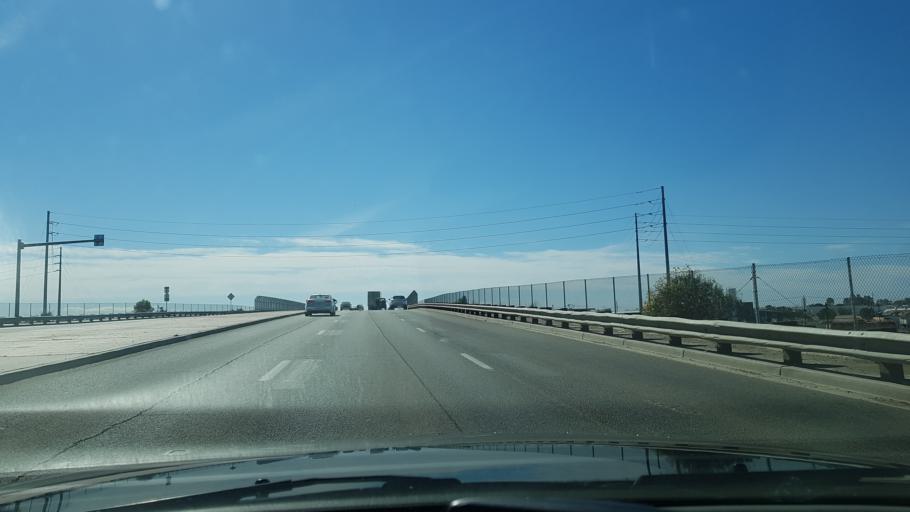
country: US
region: Arizona
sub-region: Yuma County
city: Yuma
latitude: 32.6858
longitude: -114.5816
